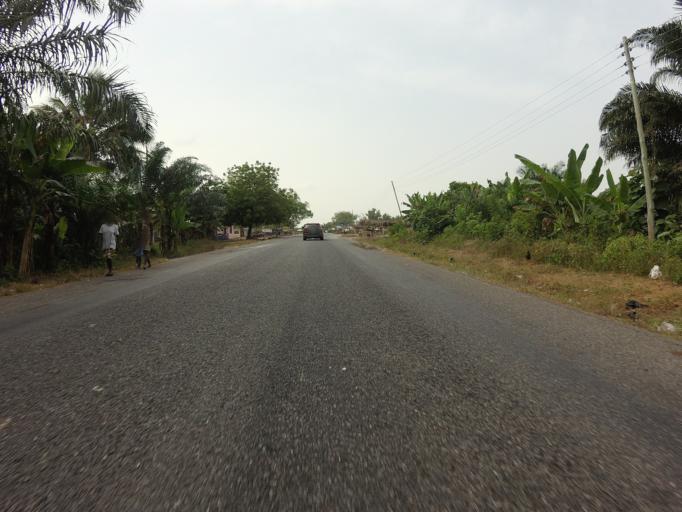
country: GH
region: Volta
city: Ho
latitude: 6.4333
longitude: 0.1913
